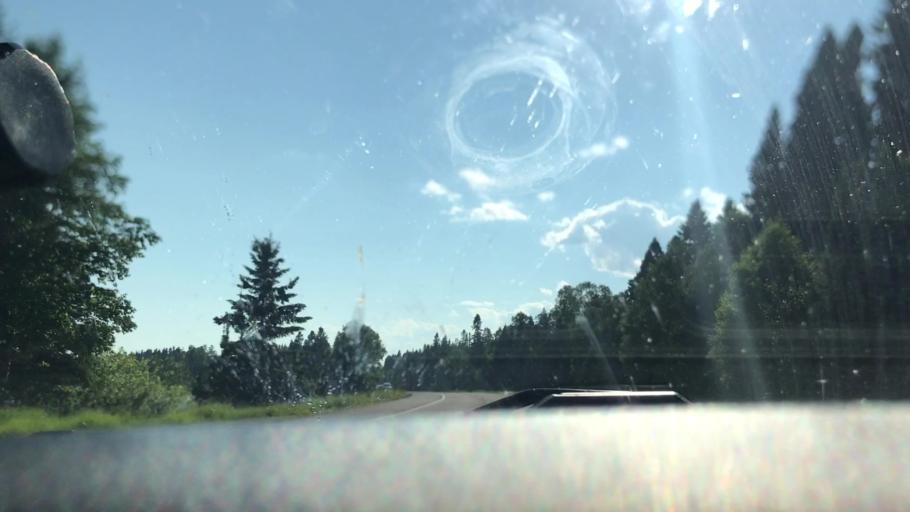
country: US
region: Minnesota
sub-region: Cook County
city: Grand Marais
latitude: 47.8119
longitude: -90.0700
